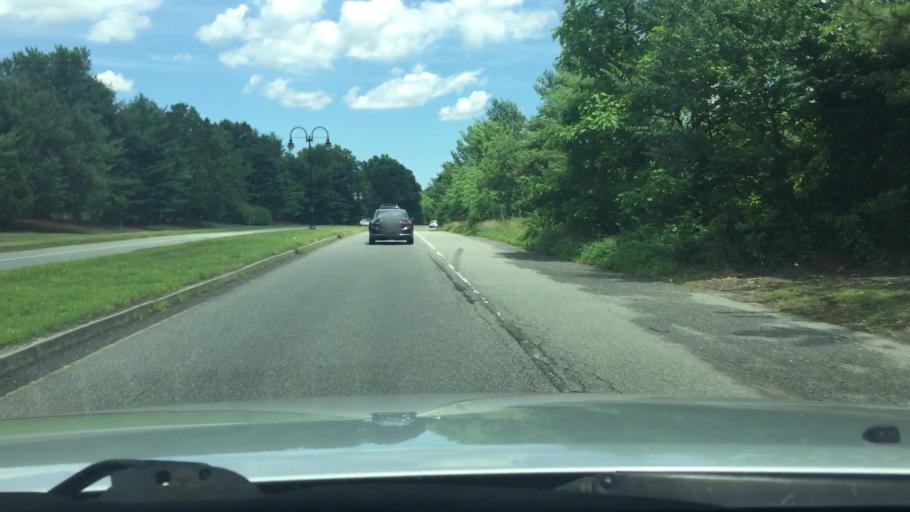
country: US
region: New Jersey
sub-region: Middlesex County
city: East Brunswick
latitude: 40.4192
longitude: -74.4065
